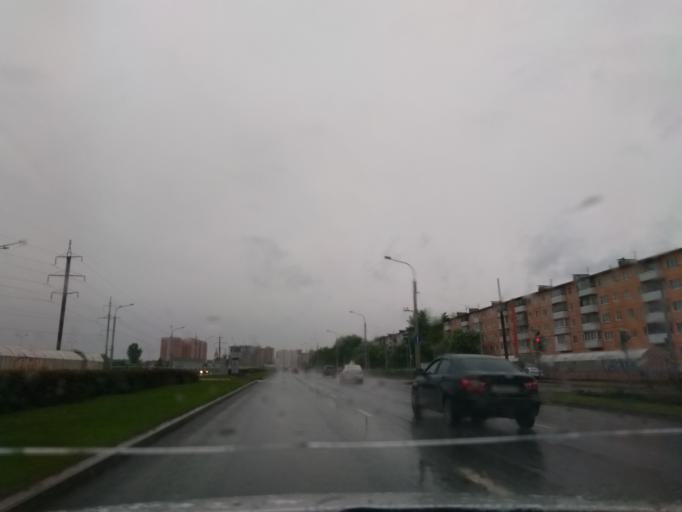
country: RU
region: Perm
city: Perm
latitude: 57.9930
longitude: 56.2992
